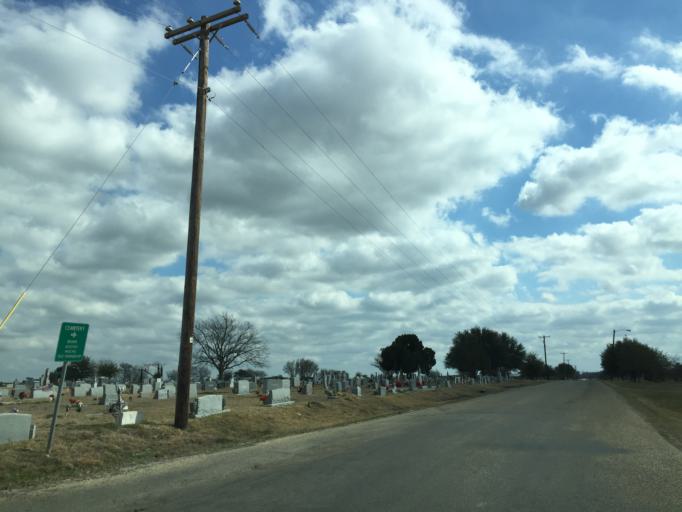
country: US
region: Texas
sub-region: Williamson County
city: Granger
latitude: 30.7195
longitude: -97.4268
